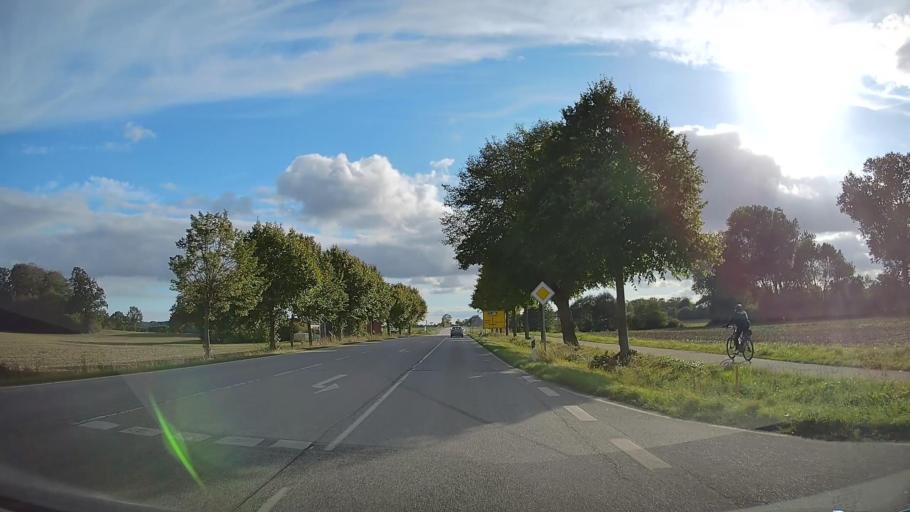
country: DE
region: Schleswig-Holstein
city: Rabel
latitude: 54.7140
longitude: 9.9508
